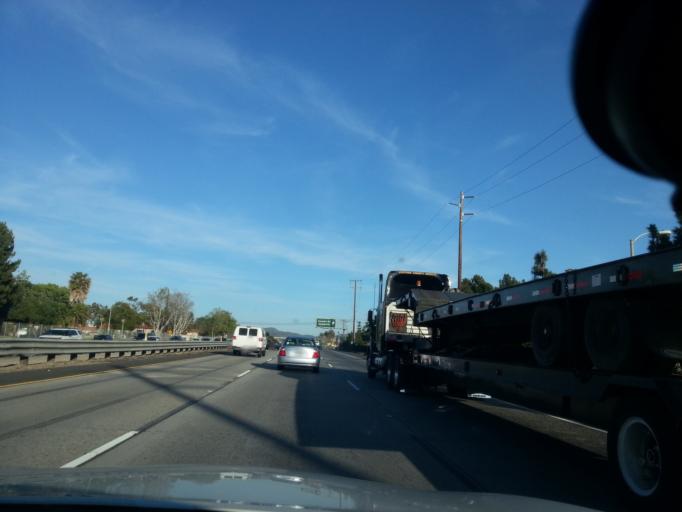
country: US
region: California
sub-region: Ventura County
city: Camarillo
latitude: 34.2181
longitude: -119.0583
